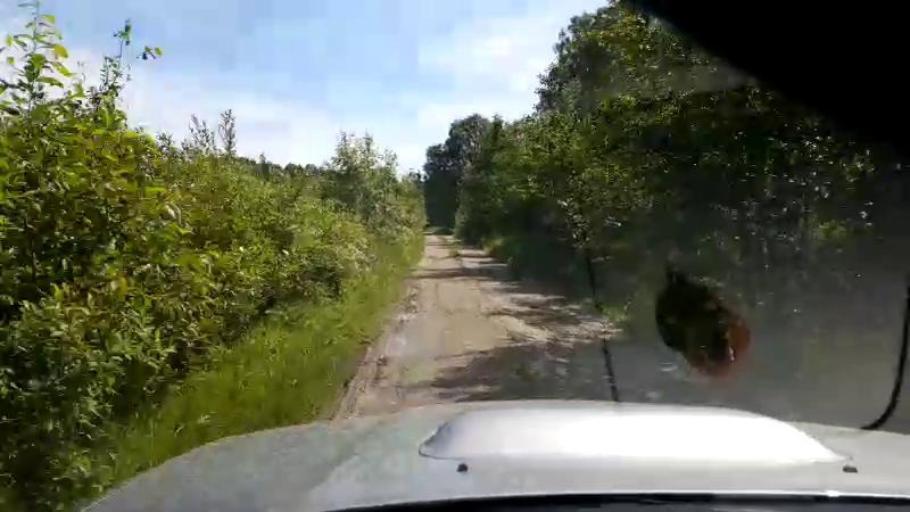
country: EE
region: Paernumaa
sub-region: Sindi linn
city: Sindi
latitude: 58.5329
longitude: 24.6608
